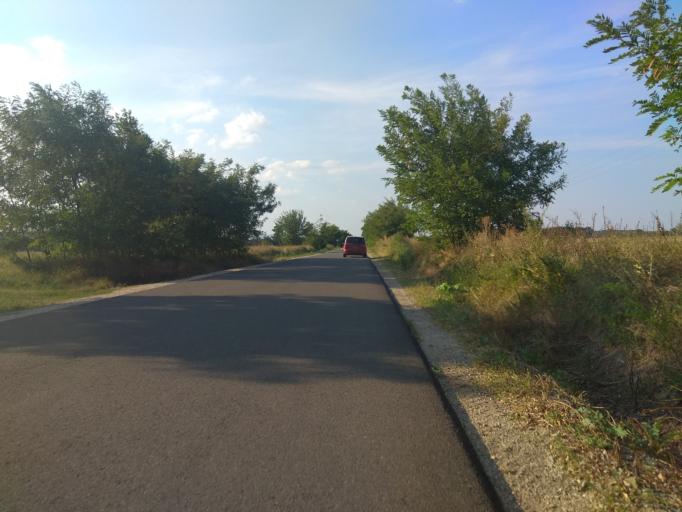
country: HU
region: Borsod-Abauj-Zemplen
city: Harsany
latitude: 47.8993
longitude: 20.7455
